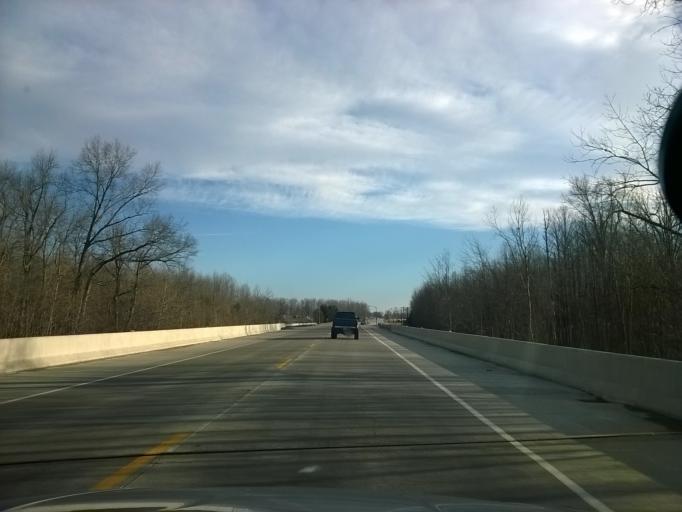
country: US
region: Indiana
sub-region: Scott County
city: Austin
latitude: 38.7632
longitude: -85.8174
